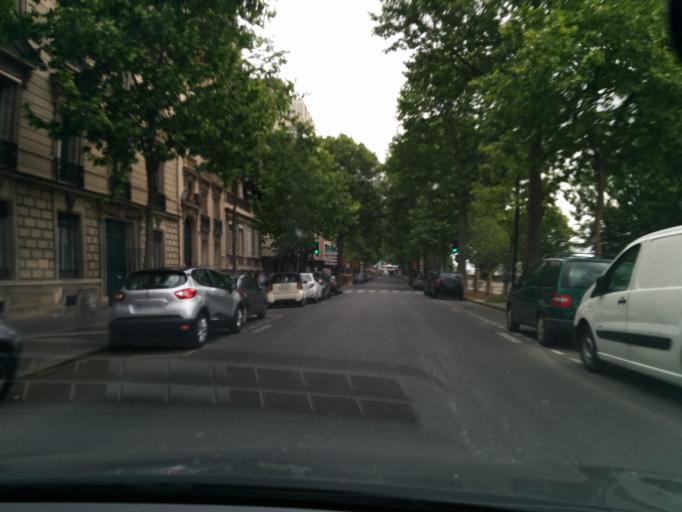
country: FR
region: Ile-de-France
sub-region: Paris
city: Paris
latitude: 48.8493
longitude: 2.3618
